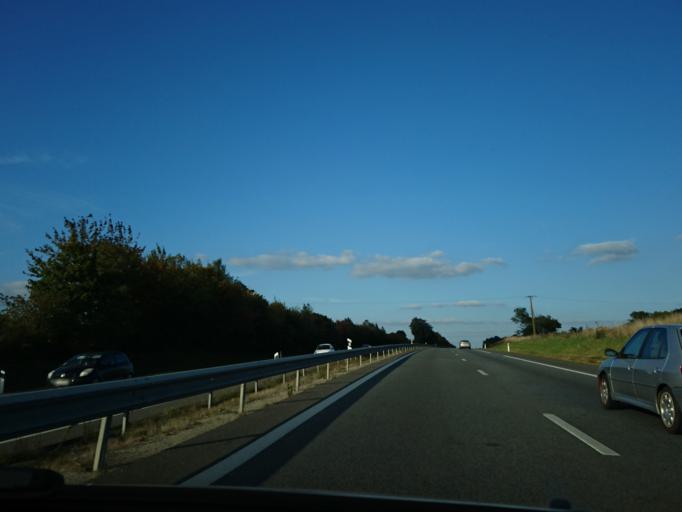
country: FR
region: Brittany
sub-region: Departement d'Ille-et-Vilaine
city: La Dominelais
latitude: 47.7886
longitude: -1.6959
